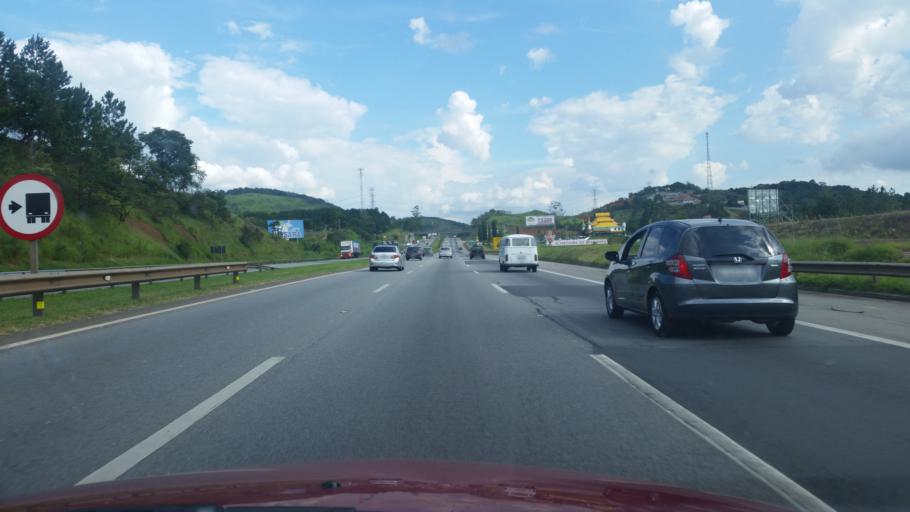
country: BR
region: Sao Paulo
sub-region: Pirapora Do Bom Jesus
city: Pirapora do Bom Jesus
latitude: -23.4799
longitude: -46.9969
